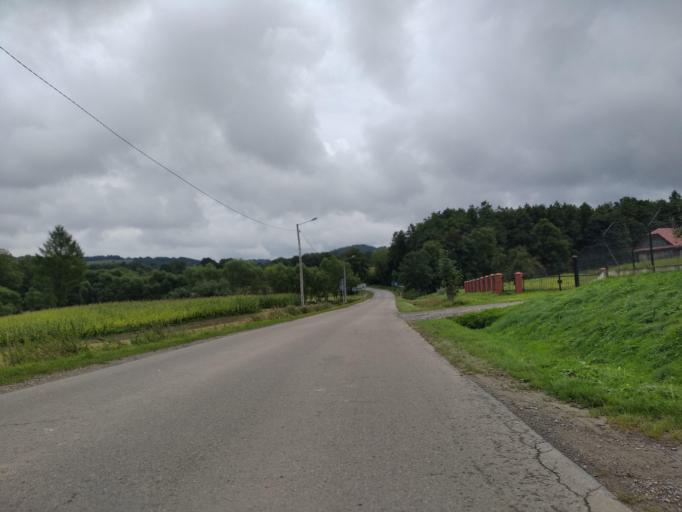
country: PL
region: Subcarpathian Voivodeship
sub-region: Powiat brzozowski
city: Nozdrzec
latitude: 49.7281
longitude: 22.2781
